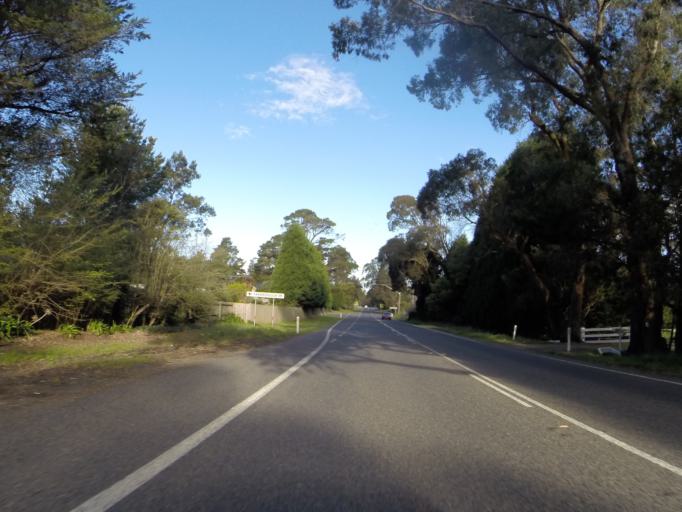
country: AU
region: New South Wales
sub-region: Wingecarribee
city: Moss Vale
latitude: -34.5612
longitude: 150.3997
